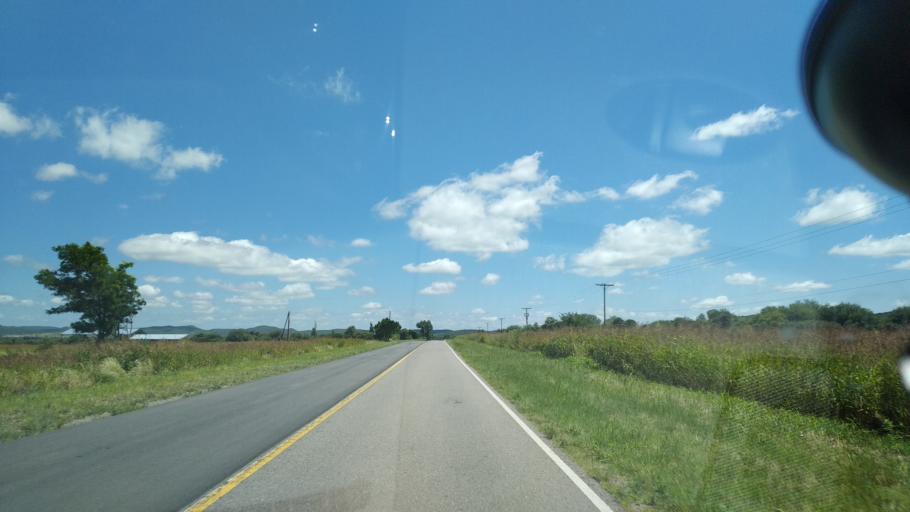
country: AR
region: Cordoba
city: Salsacate
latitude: -31.3921
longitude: -65.0985
